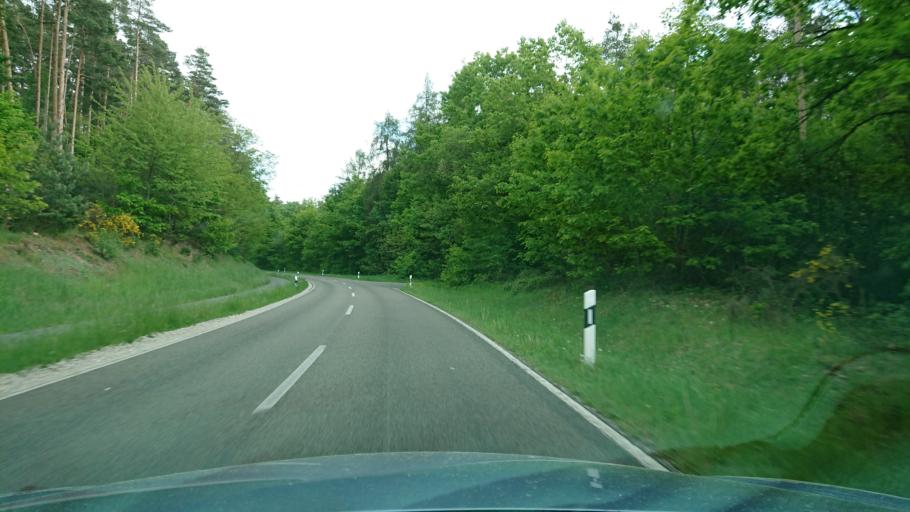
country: DE
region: Bavaria
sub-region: Regierungsbezirk Mittelfranken
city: Rottenbach
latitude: 49.6660
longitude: 10.9480
